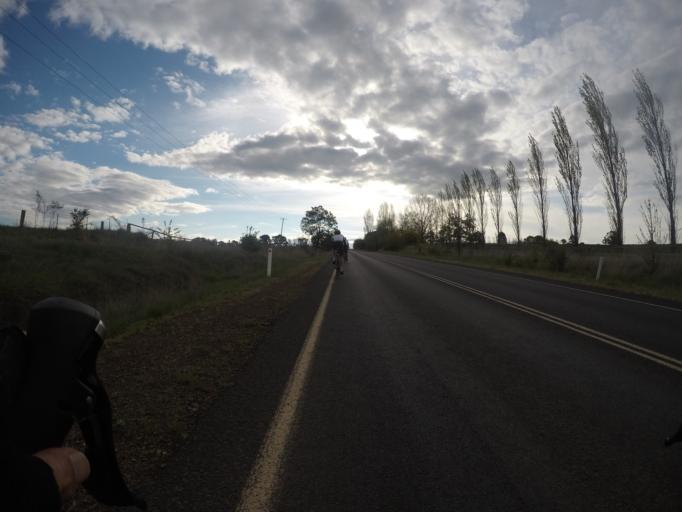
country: AU
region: New South Wales
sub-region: Orange Municipality
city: Orange
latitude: -33.2891
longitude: 149.0325
